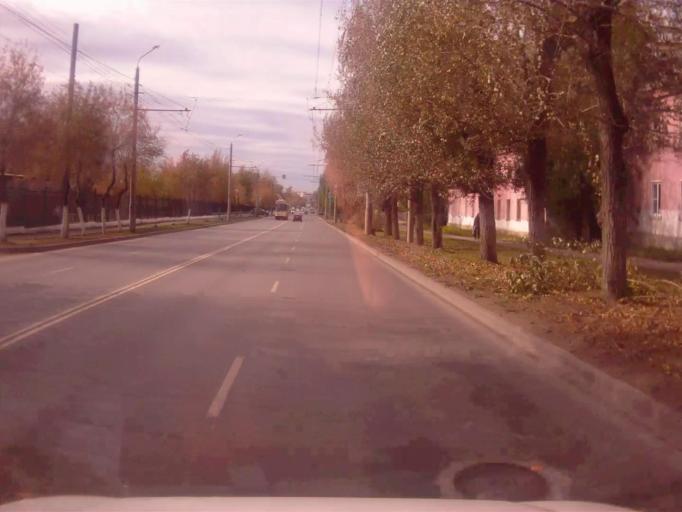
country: RU
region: Chelyabinsk
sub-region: Gorod Chelyabinsk
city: Chelyabinsk
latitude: 55.1123
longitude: 61.4640
